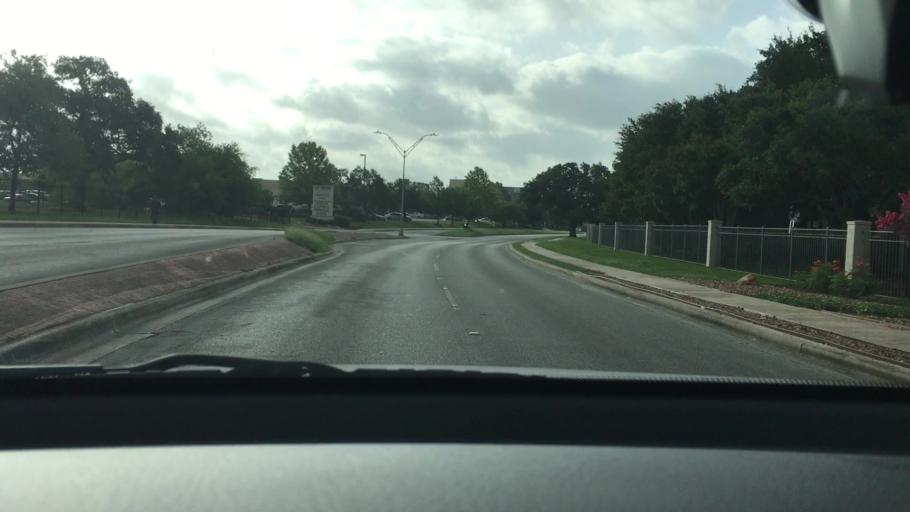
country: US
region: Texas
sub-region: Bexar County
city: Hollywood Park
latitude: 29.6038
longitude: -98.4633
